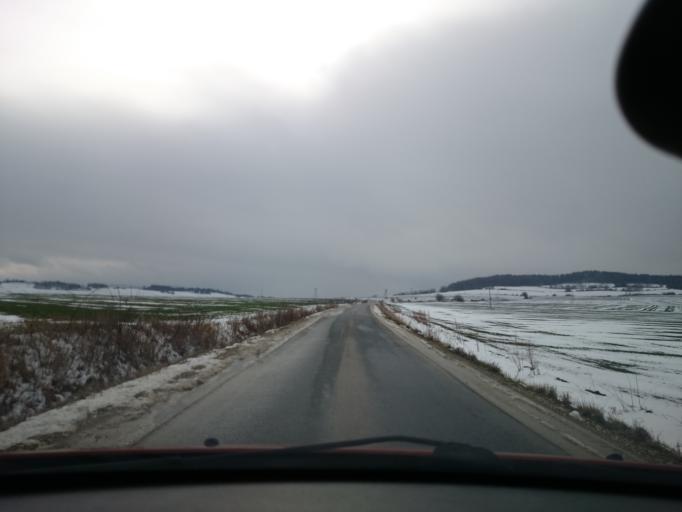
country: PL
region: Lower Silesian Voivodeship
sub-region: Powiat zabkowicki
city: Zabkowice Slaskie
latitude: 50.5627
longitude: 16.7855
